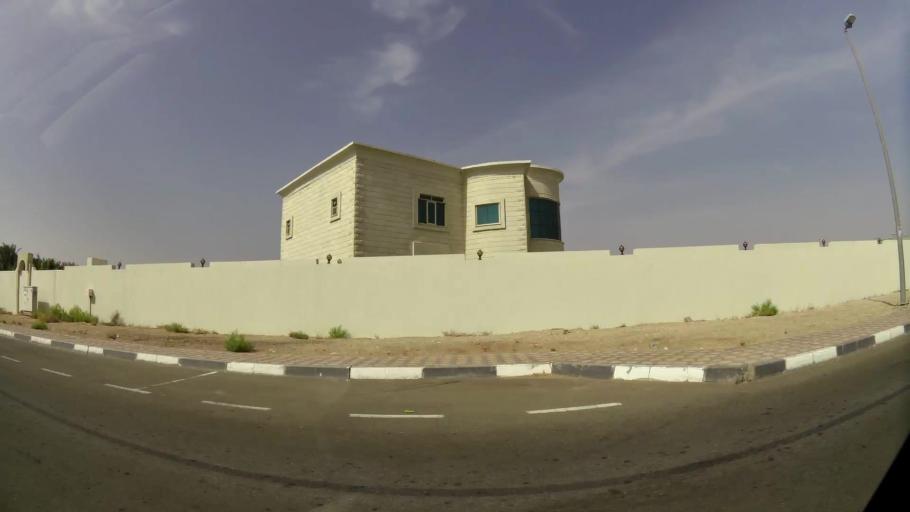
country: AE
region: Abu Dhabi
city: Al Ain
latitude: 24.1474
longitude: 55.6988
